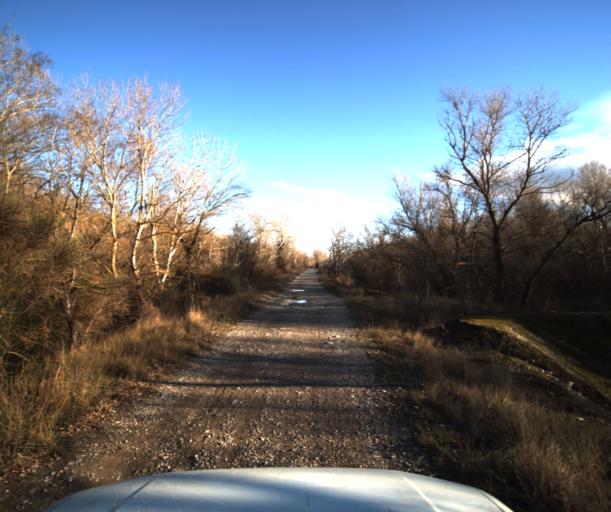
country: FR
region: Provence-Alpes-Cote d'Azur
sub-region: Departement des Bouches-du-Rhone
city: Le Puy-Sainte-Reparade
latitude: 43.6752
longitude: 5.4688
